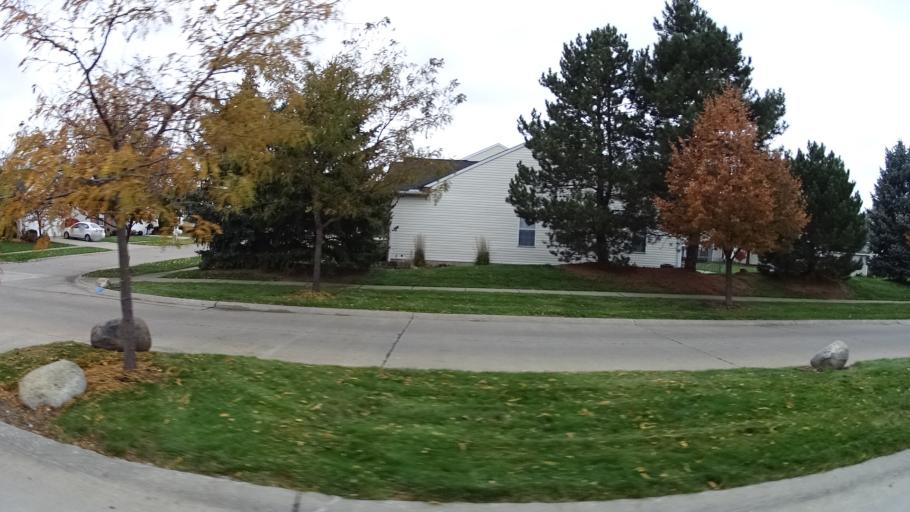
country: US
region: Ohio
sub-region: Lorain County
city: Amherst
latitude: 41.4284
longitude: -82.2266
